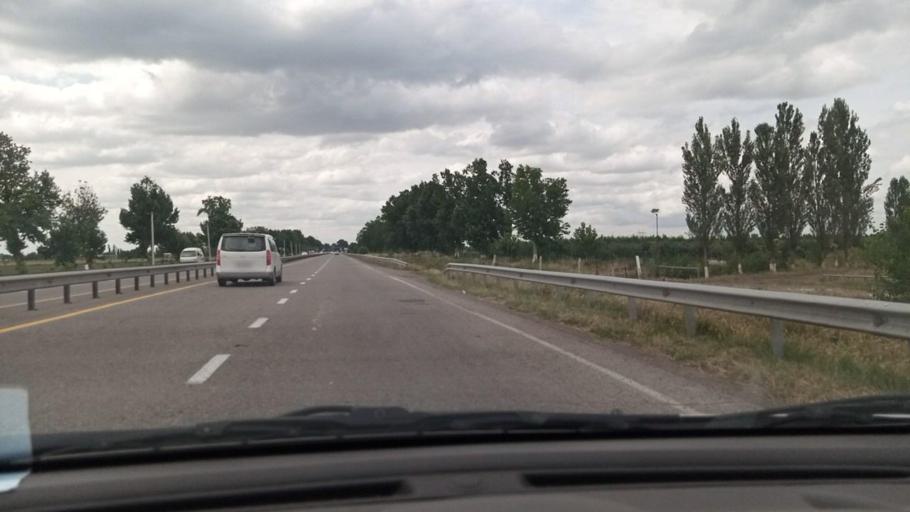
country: UZ
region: Toshkent Shahri
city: Bektemir
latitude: 41.1725
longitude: 69.4128
